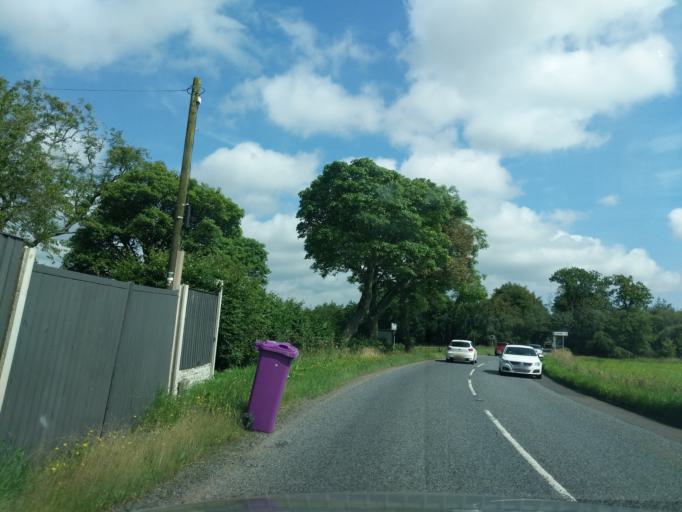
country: GB
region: Scotland
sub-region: Angus
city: Muirhead
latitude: 56.5068
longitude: -3.1454
